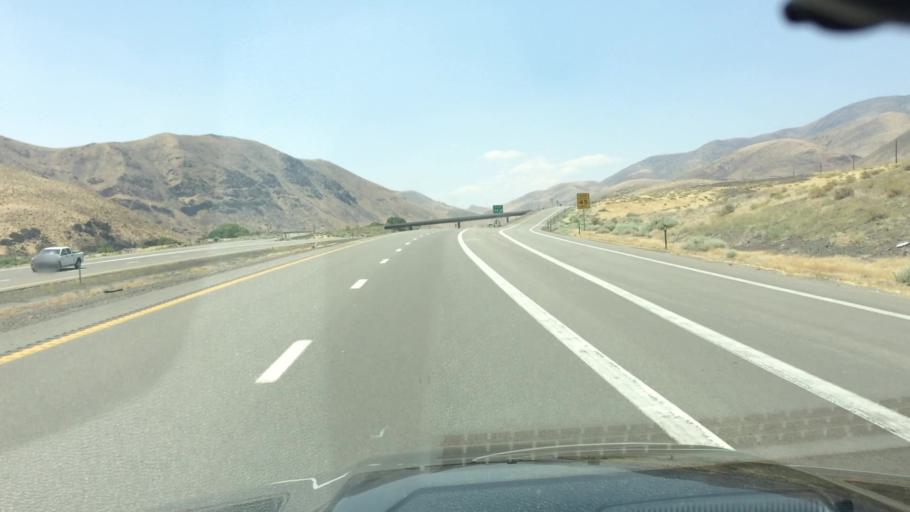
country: US
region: Nevada
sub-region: Lyon County
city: Fernley
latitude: 39.5897
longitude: -119.4243
